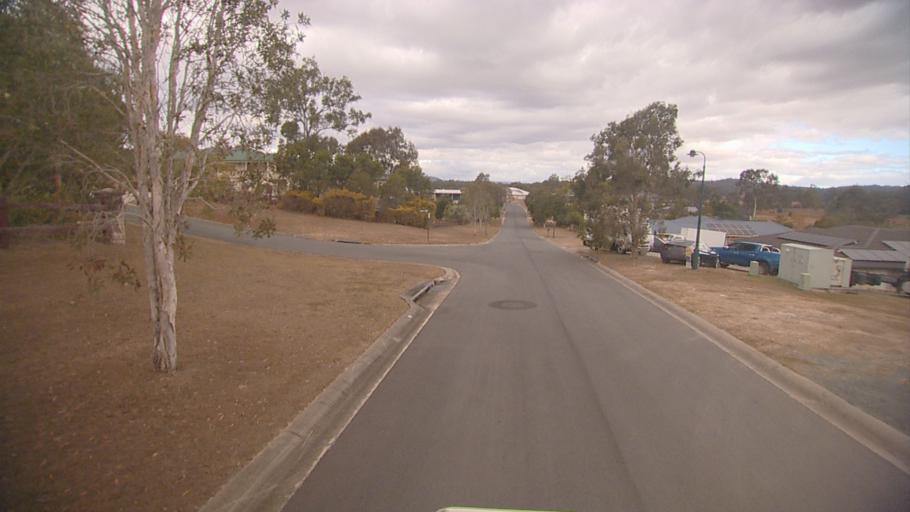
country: AU
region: Queensland
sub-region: Logan
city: Cedar Vale
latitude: -27.8762
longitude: 153.0729
